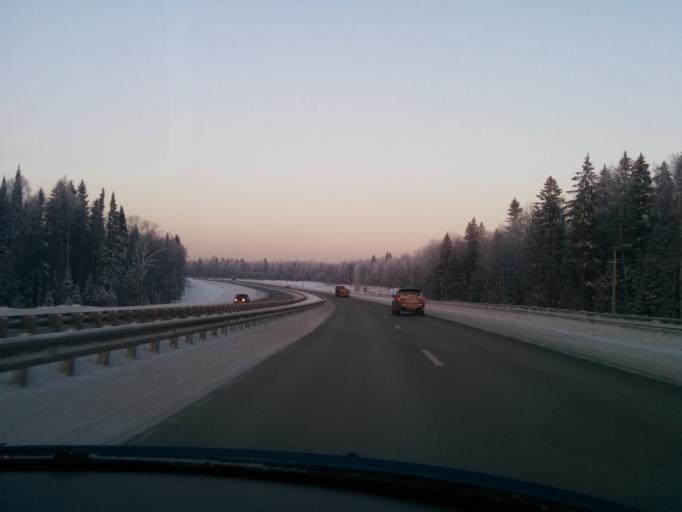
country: RU
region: Perm
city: Ferma
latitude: 58.0288
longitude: 56.4306
